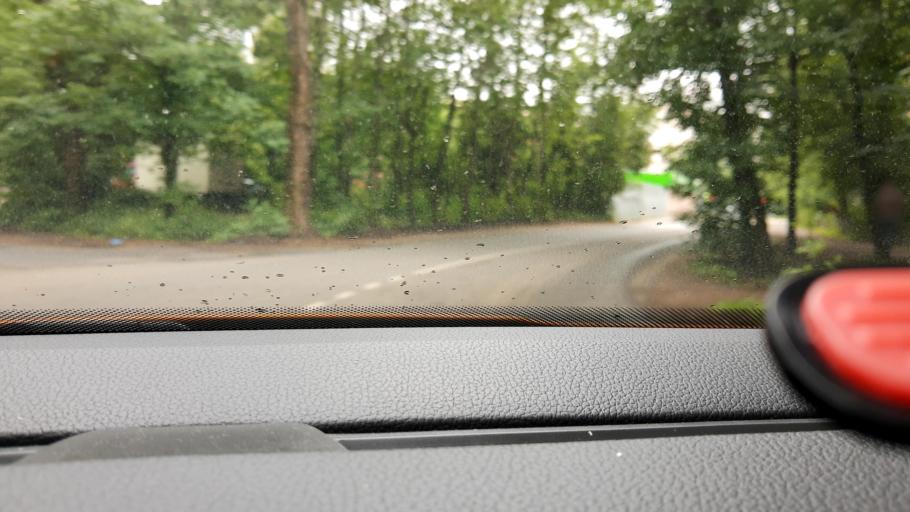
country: RU
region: Moskovskaya
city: Pushkino
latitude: 56.0128
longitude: 37.8654
